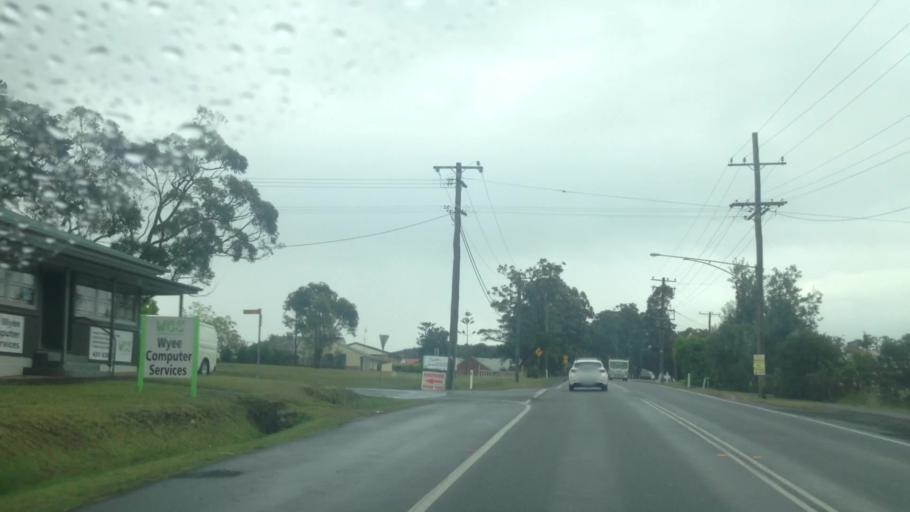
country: AU
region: New South Wales
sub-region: Wyong Shire
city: Charmhaven
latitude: -33.1701
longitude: 151.4769
